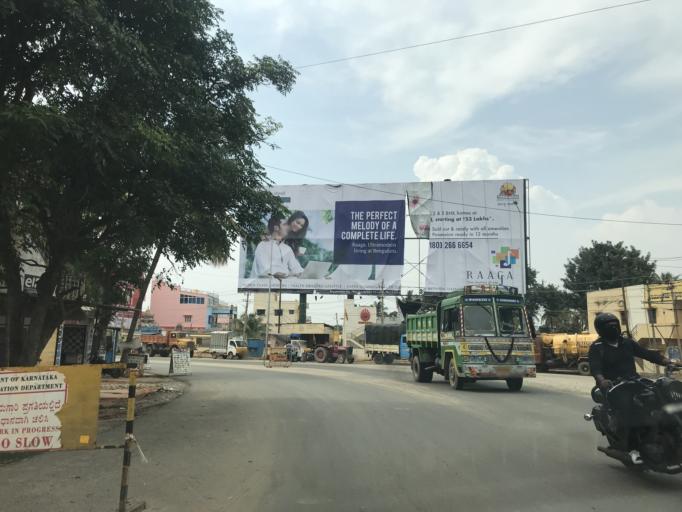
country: IN
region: Karnataka
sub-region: Bangalore Urban
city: Yelahanka
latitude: 13.0921
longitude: 77.6548
